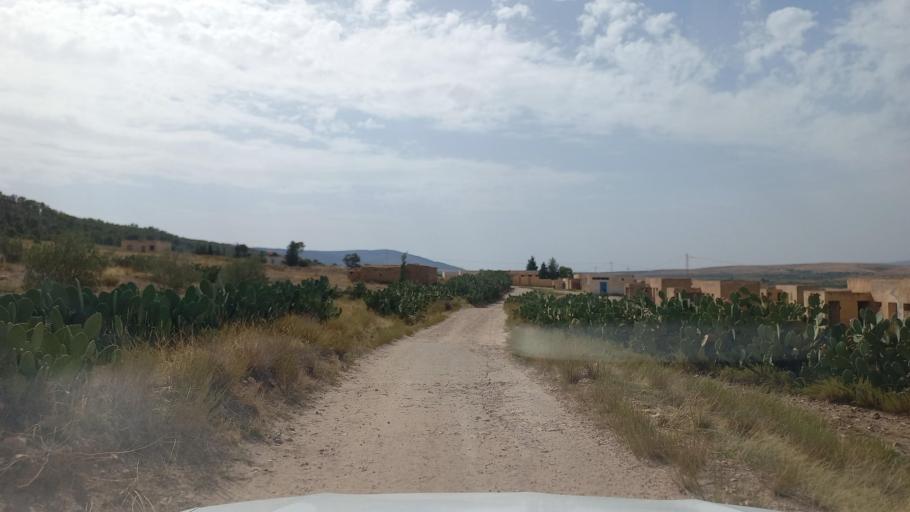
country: TN
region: Al Qasrayn
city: Kasserine
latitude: 35.3541
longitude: 8.8878
